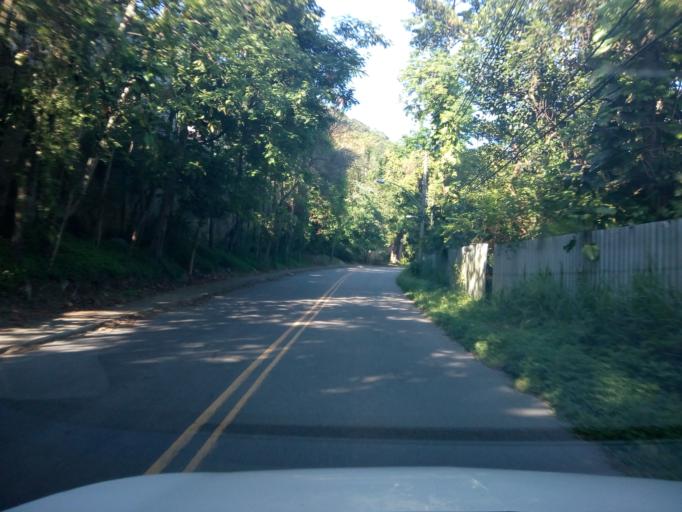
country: BR
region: Rio de Janeiro
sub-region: Nilopolis
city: Nilopolis
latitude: -23.0251
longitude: -43.5031
